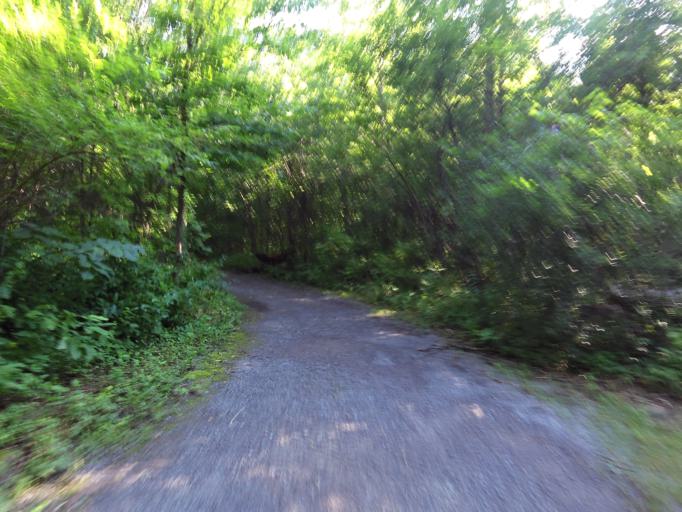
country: CA
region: Ontario
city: Bells Corners
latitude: 45.3491
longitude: -75.8574
